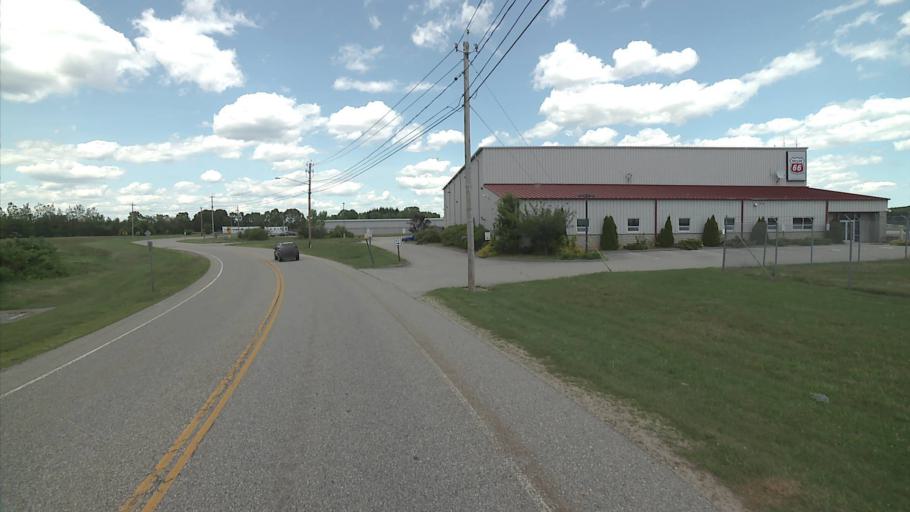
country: US
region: Connecticut
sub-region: New London County
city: Poquonock Bridge
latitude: 41.3352
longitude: -72.0430
